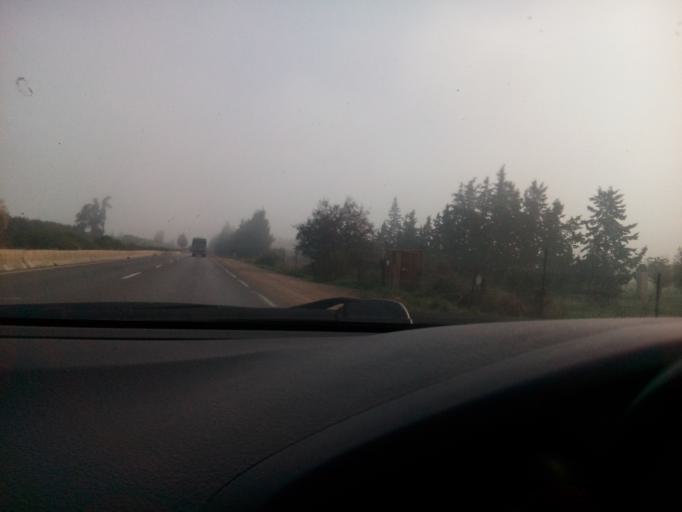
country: DZ
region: Oran
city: Mers el Kebir
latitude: 35.6029
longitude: -0.7640
